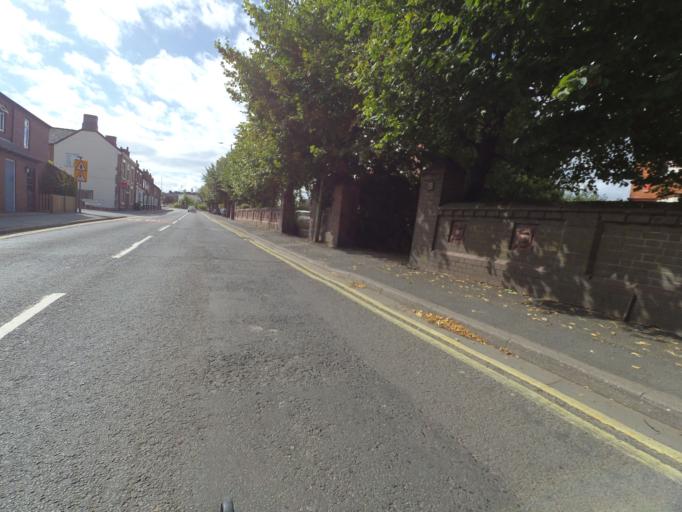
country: GB
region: England
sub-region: Telford and Wrekin
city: Newport
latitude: 52.7653
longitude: -2.3766
